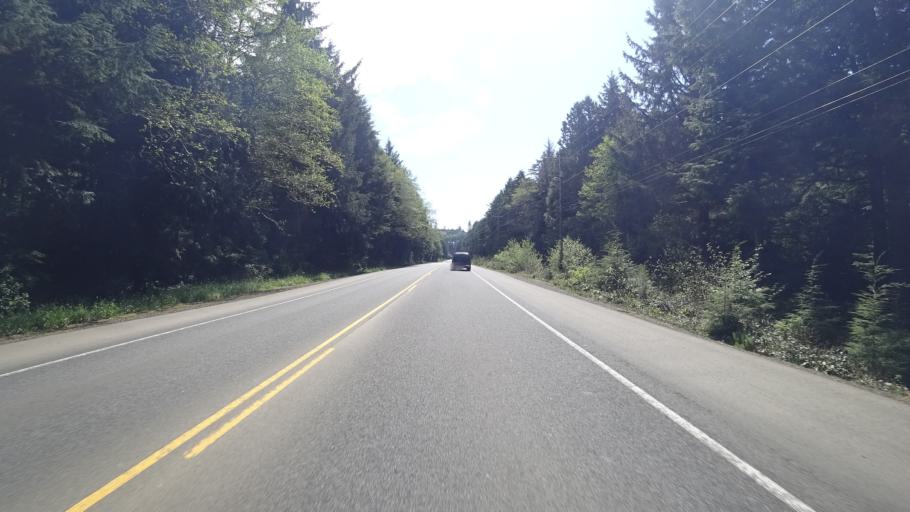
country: US
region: Oregon
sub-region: Lincoln County
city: Lincoln Beach
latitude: 44.8345
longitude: -124.0544
